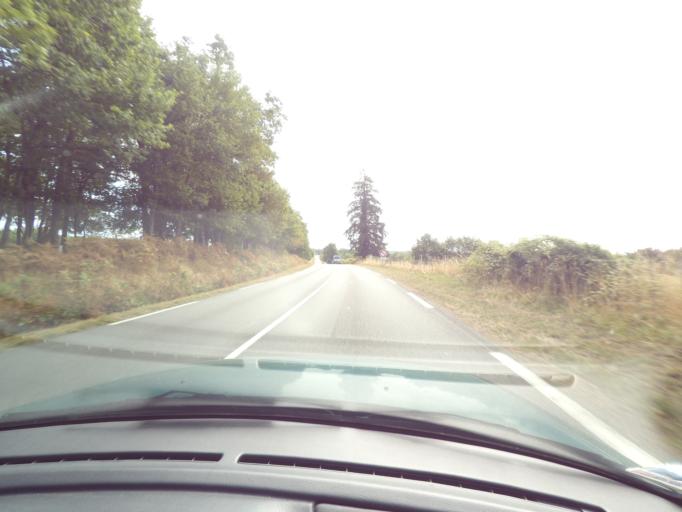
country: FR
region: Limousin
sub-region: Departement de la Haute-Vienne
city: Feytiat
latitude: 45.8028
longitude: 1.3759
